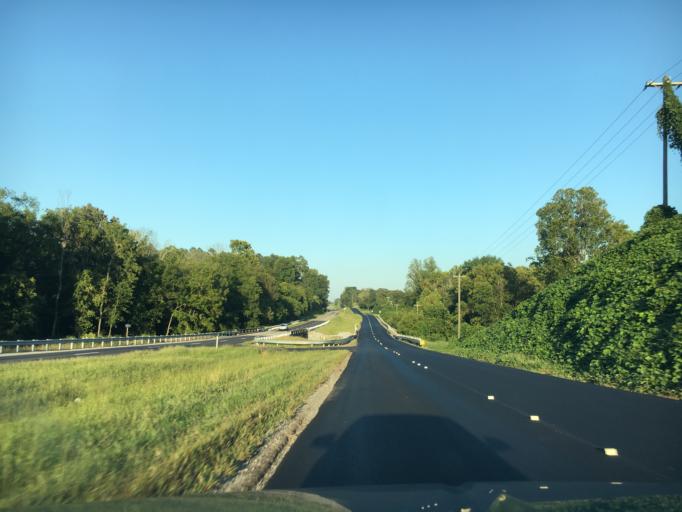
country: US
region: Virginia
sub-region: City of Danville
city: Danville
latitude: 36.5806
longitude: -79.2258
